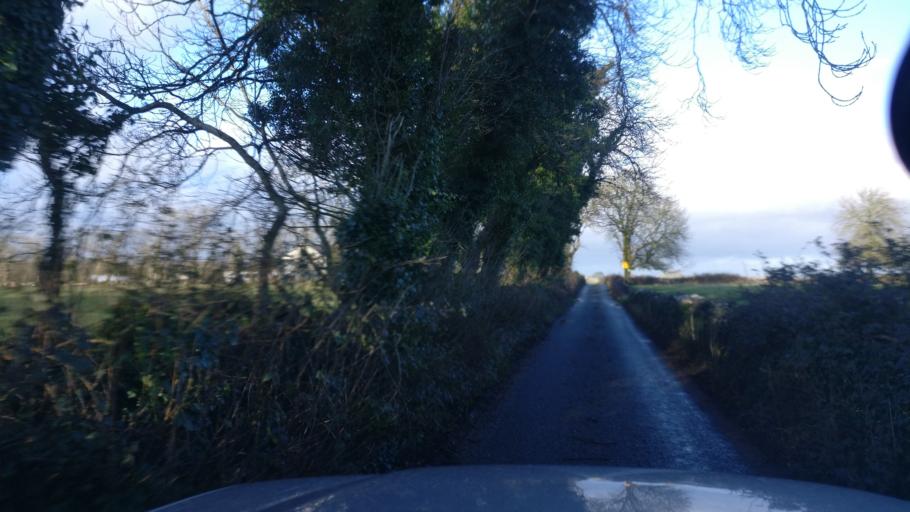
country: IE
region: Connaught
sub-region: County Galway
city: Loughrea
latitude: 53.2315
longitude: -8.5767
